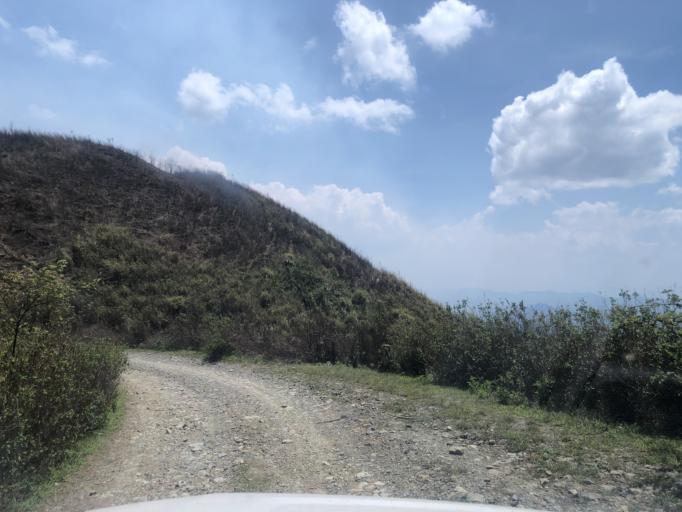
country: LA
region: Phongsali
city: Phongsali
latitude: 21.4111
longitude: 102.1864
